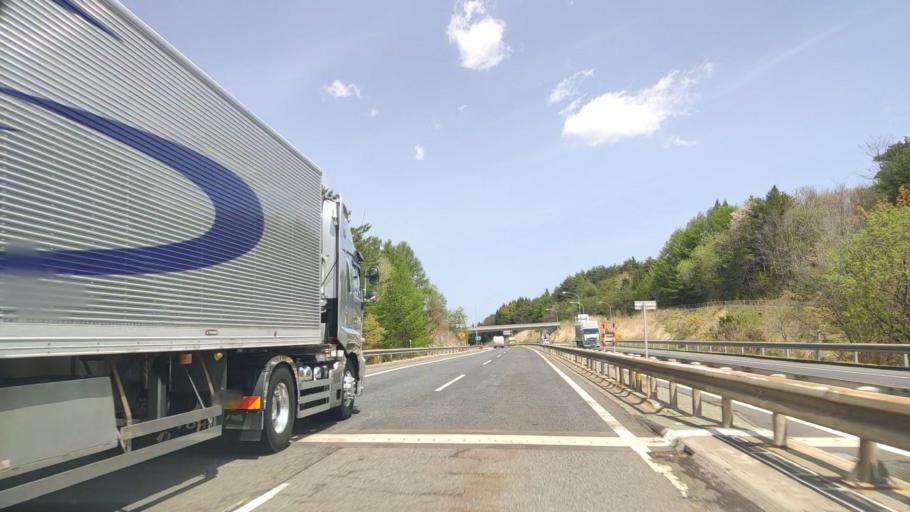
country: JP
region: Aomori
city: Hachinohe
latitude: 40.4074
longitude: 141.4436
